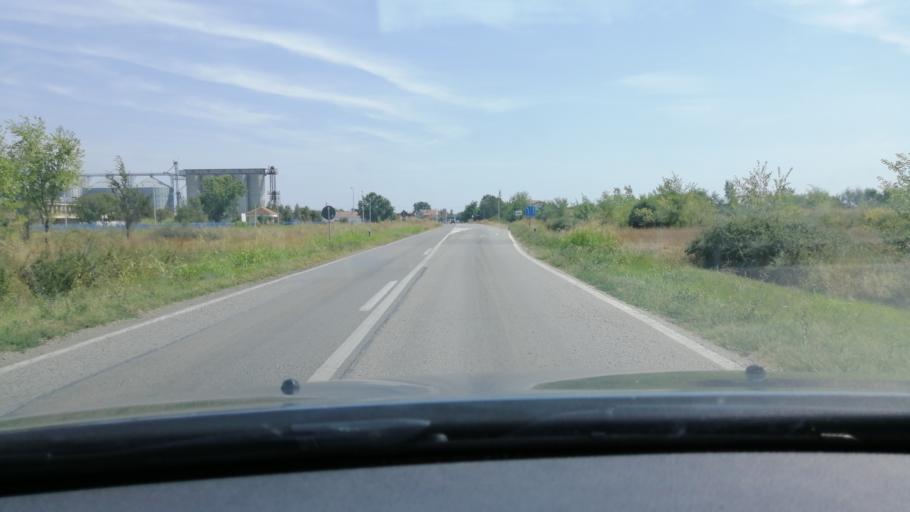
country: RS
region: Autonomna Pokrajina Vojvodina
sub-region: Srednjebanatski Okrug
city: Secanj
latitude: 45.3698
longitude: 20.7568
